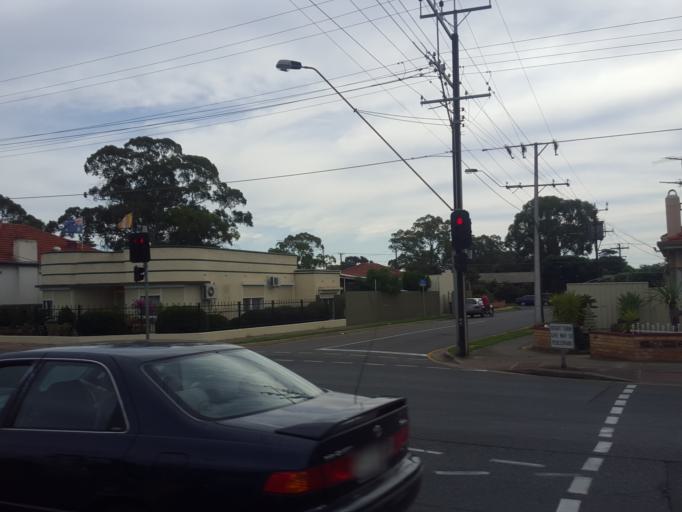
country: AU
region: South Australia
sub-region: Charles Sturt
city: Woodville North
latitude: -34.8723
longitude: 138.5482
